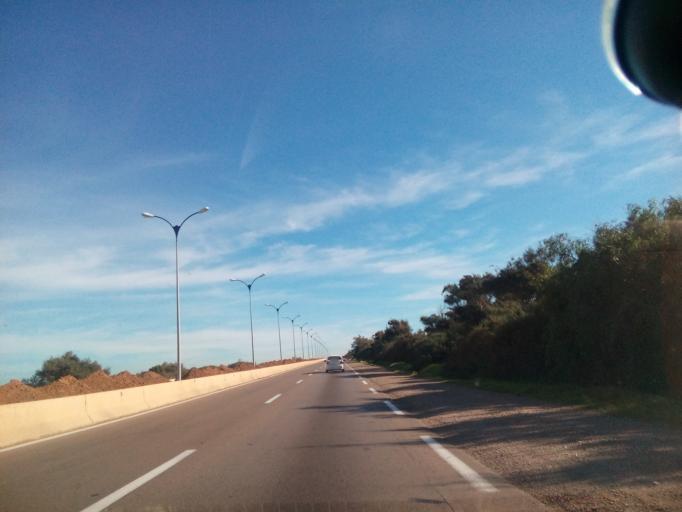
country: DZ
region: Mostaganem
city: Mostaganem
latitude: 35.8010
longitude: -0.0748
